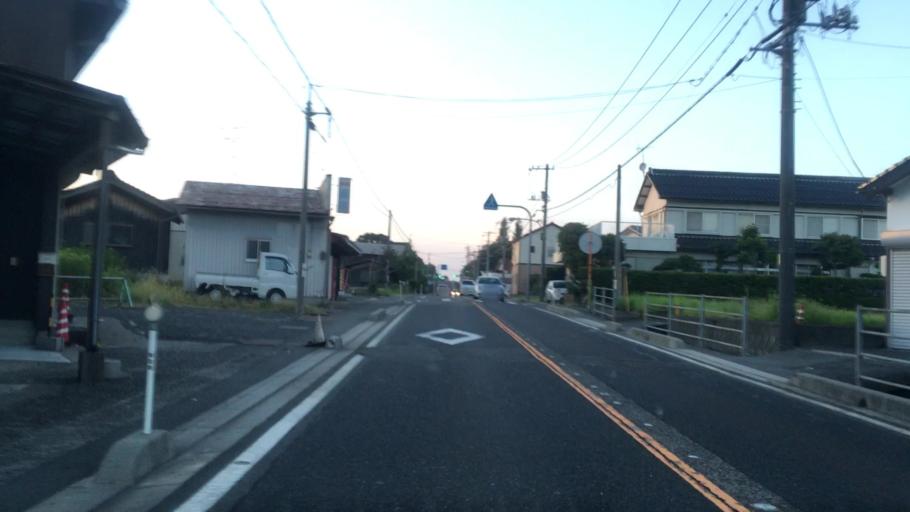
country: JP
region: Tottori
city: Tottori
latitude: 35.5845
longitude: 134.3326
